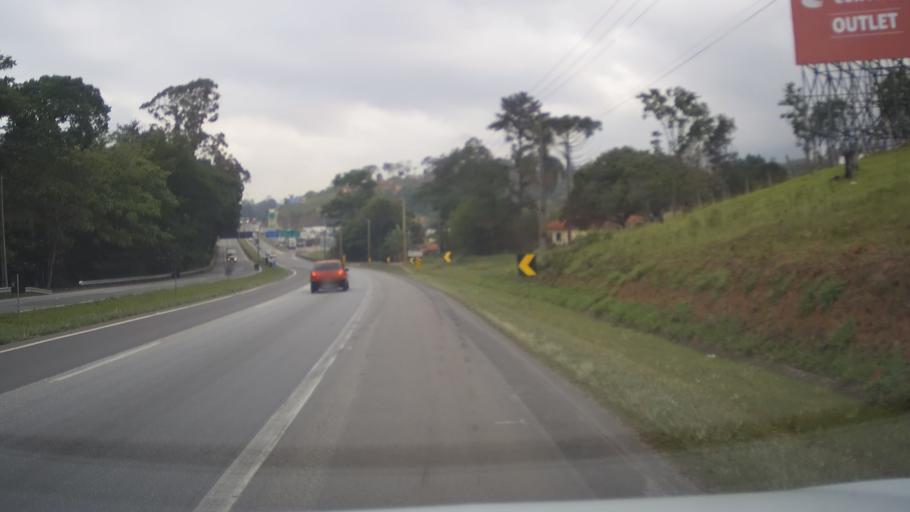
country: BR
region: Minas Gerais
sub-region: Extrema
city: Extrema
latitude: -22.8807
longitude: -46.3746
